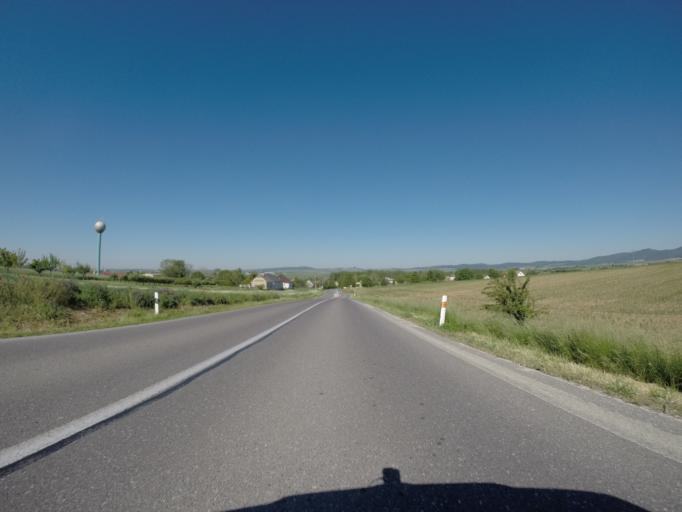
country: SK
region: Trnavsky
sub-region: Okres Trnava
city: Piestany
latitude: 48.5158
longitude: 18.0211
